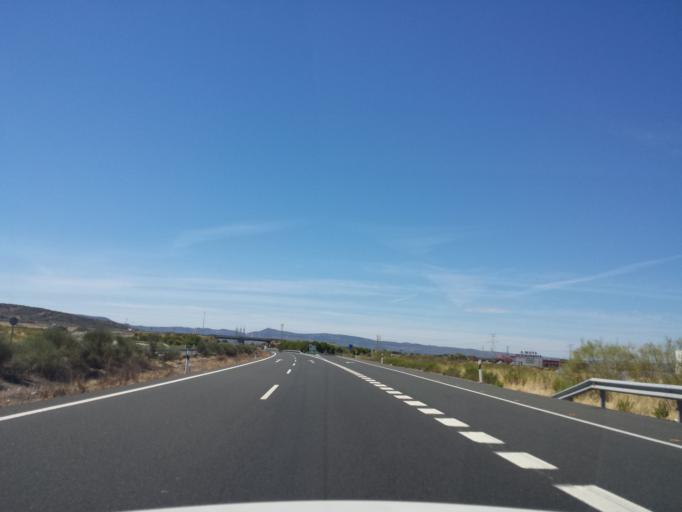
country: ES
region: Extremadura
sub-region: Provincia de Caceres
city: Almaraz
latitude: 39.8309
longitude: -5.6560
